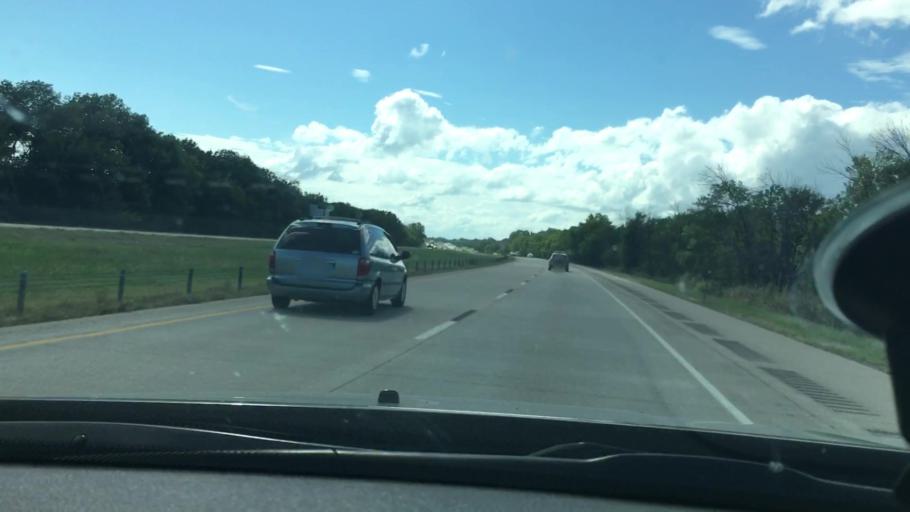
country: US
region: Oklahoma
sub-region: Muskogee County
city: Warner
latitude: 35.4876
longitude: -95.1816
